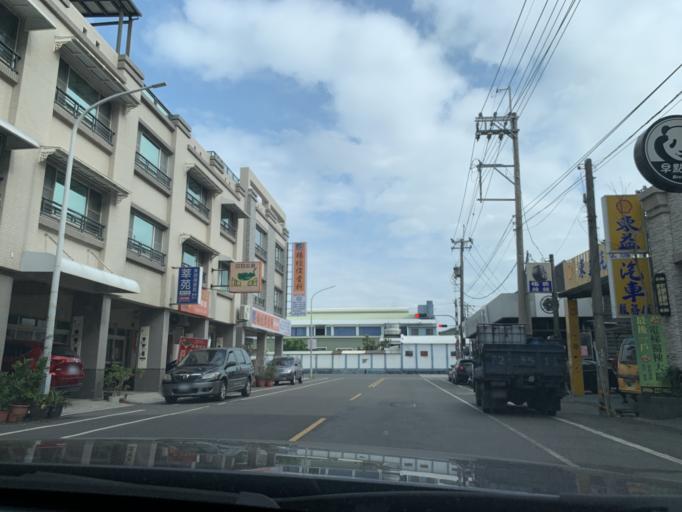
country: TW
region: Taiwan
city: Fengshan
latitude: 22.4663
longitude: 120.4625
